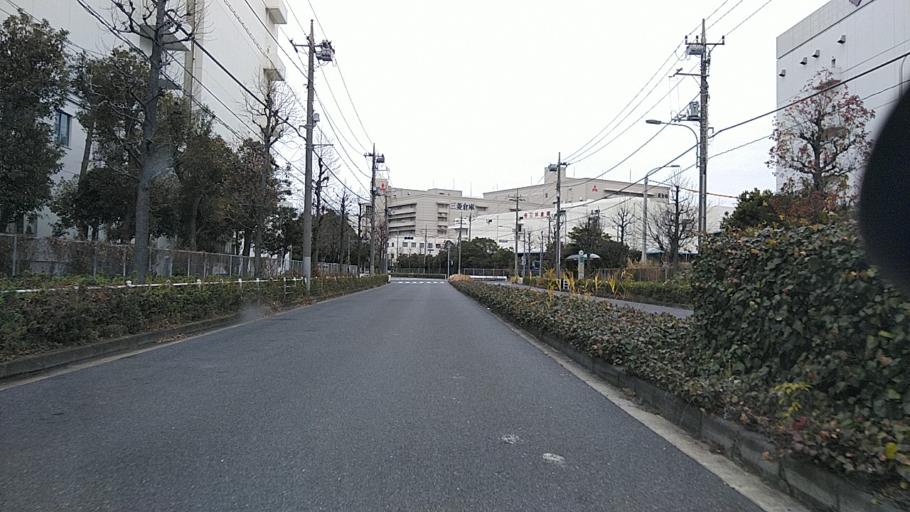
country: JP
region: Kanagawa
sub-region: Kawasaki-shi
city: Kawasaki
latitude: 35.5886
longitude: 139.7659
